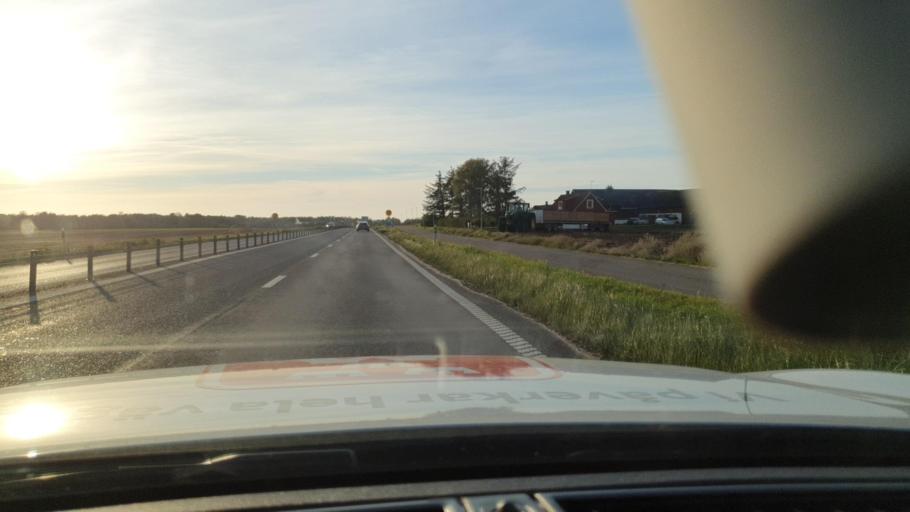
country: SE
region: Halland
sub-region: Laholms Kommun
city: Mellbystrand
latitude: 56.5038
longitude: 12.9786
